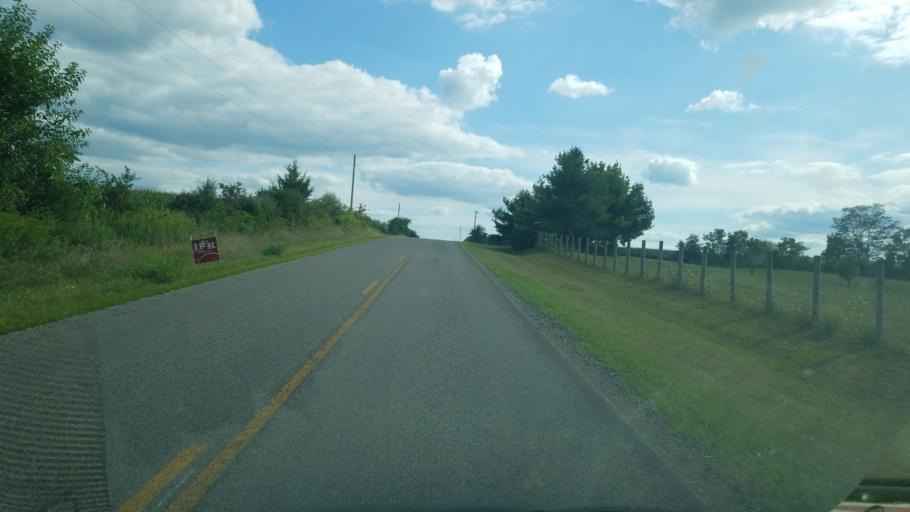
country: US
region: Ohio
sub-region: Logan County
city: De Graff
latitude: 40.2887
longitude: -83.9247
